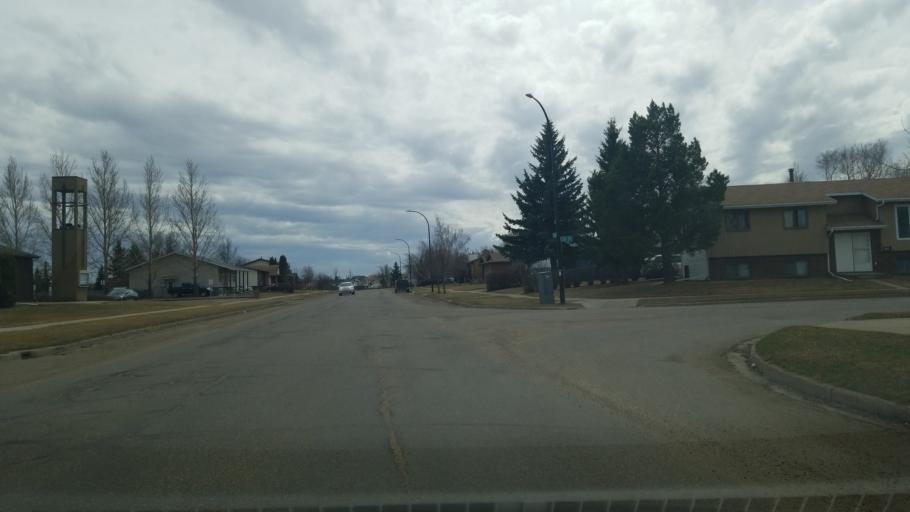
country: CA
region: Saskatchewan
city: Lloydminster
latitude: 53.2659
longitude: -110.0255
